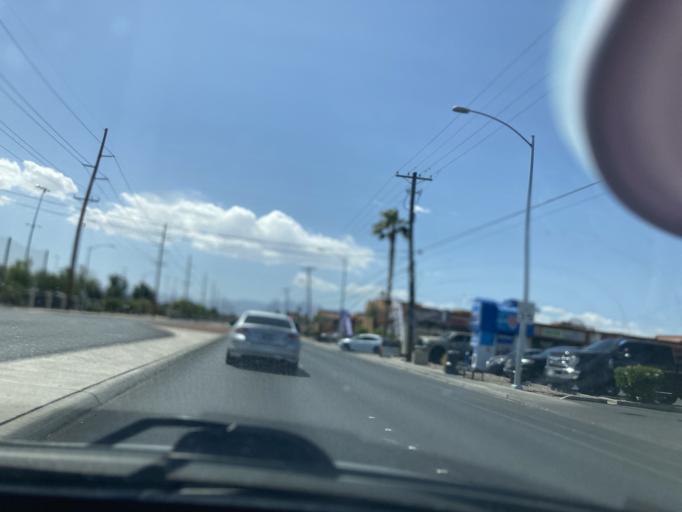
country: US
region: Nevada
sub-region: Clark County
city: North Las Vegas
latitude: 36.1811
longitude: -115.0988
